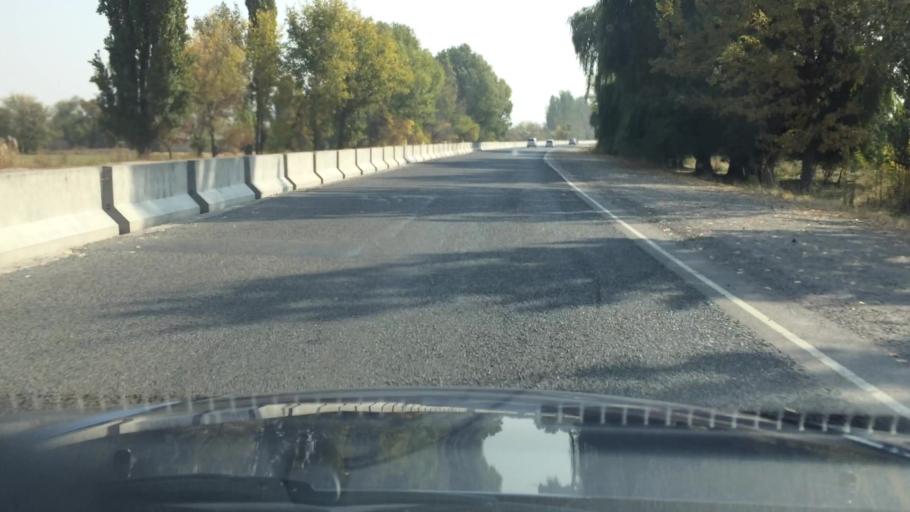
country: KG
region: Chuy
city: Kant
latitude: 42.9753
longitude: 74.8929
